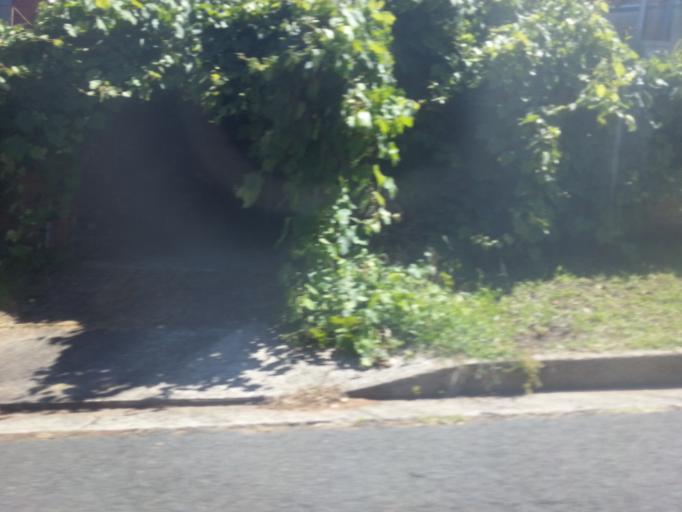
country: AU
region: New South Wales
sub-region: Wollongong
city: Mangerton
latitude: -34.4372
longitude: 150.8791
